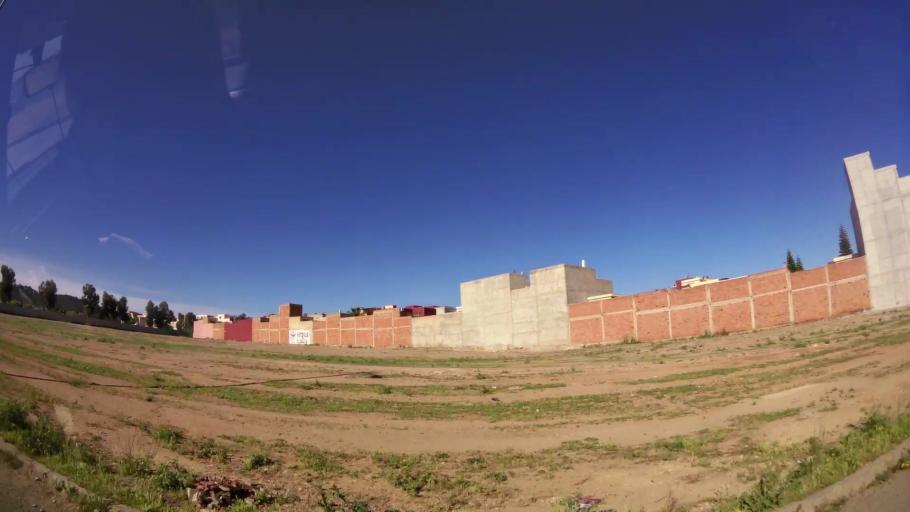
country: MA
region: Oriental
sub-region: Oujda-Angad
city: Oujda
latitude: 34.6545
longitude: -1.8898
